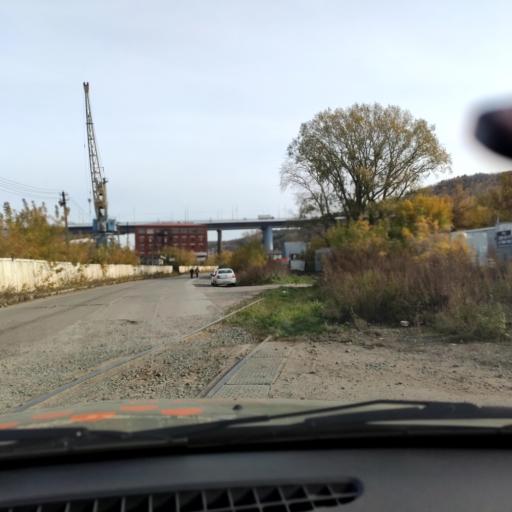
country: RU
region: Bashkortostan
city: Ufa
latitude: 54.7543
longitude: 55.9633
